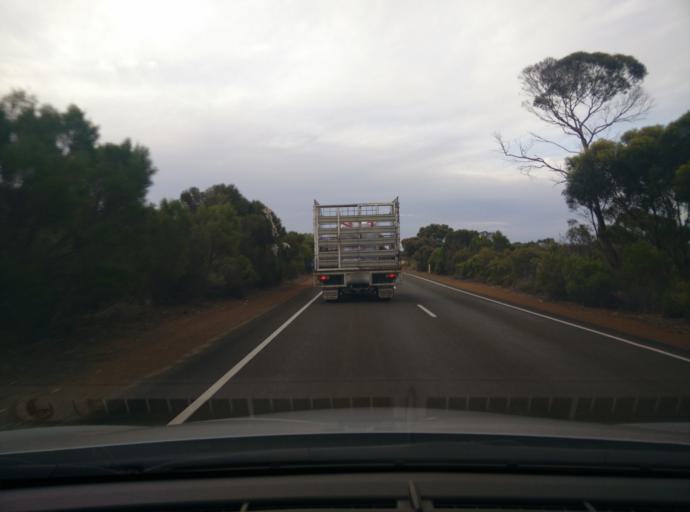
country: AU
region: South Australia
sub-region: Kangaroo Island
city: Kingscote
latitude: -35.7455
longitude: 137.5870
